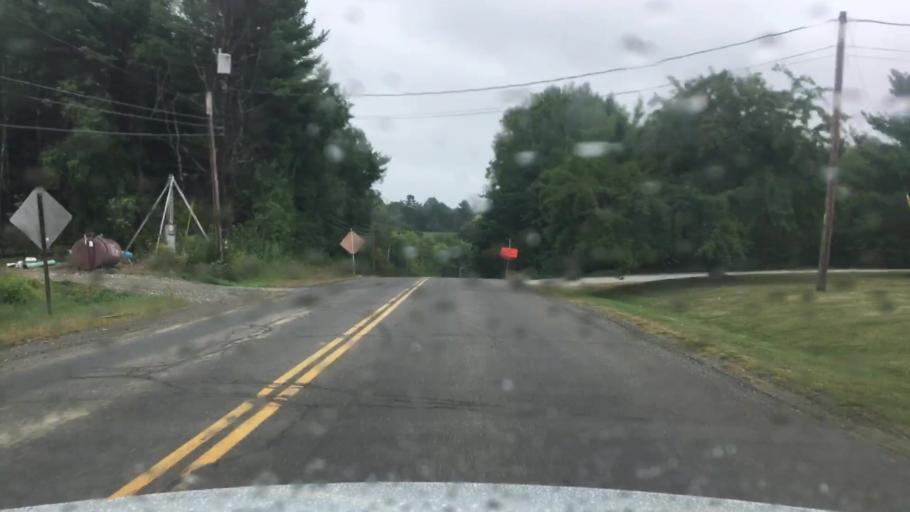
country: US
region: Maine
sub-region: Penobscot County
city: Hampden
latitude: 44.7535
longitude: -68.8378
